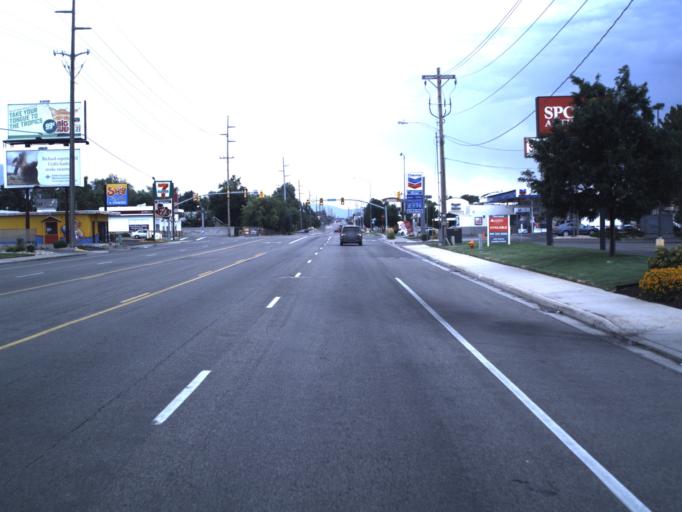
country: US
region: Utah
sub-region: Salt Lake County
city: Murray
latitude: 40.6509
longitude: -111.8660
